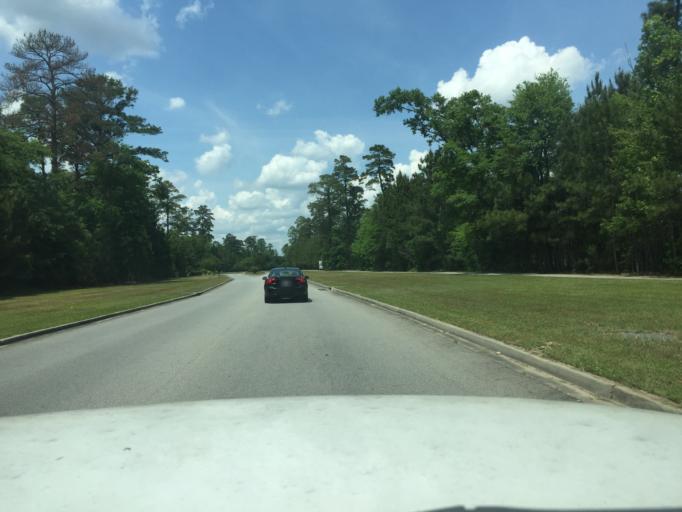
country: US
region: Georgia
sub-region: Chatham County
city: Georgetown
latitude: 32.0375
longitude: -81.2315
